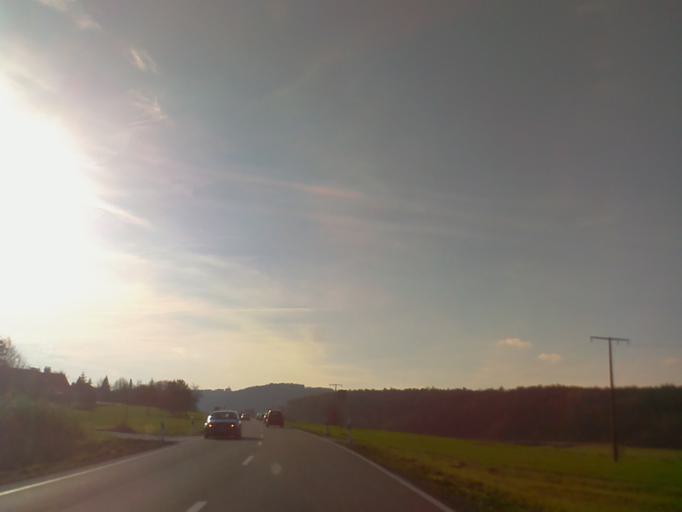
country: DE
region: Bavaria
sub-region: Regierungsbezirk Unterfranken
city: Kreuzwertheim
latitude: 49.7791
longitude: 9.5376
